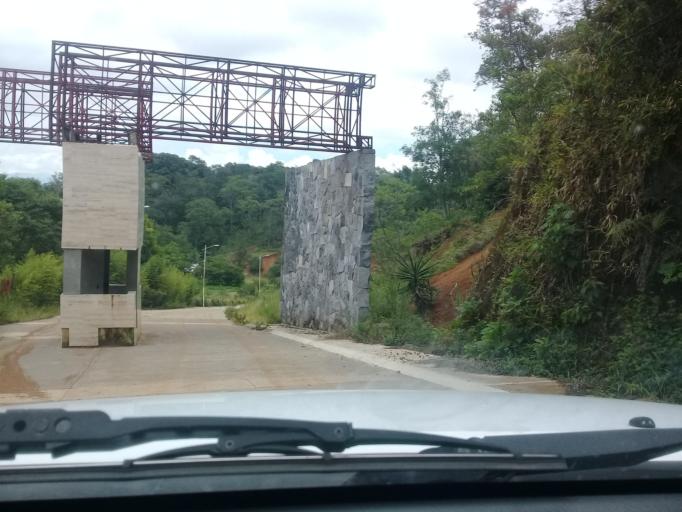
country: MX
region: Veracruz
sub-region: Xalapa
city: Lomas Verdes
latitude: 19.5021
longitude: -96.9124
